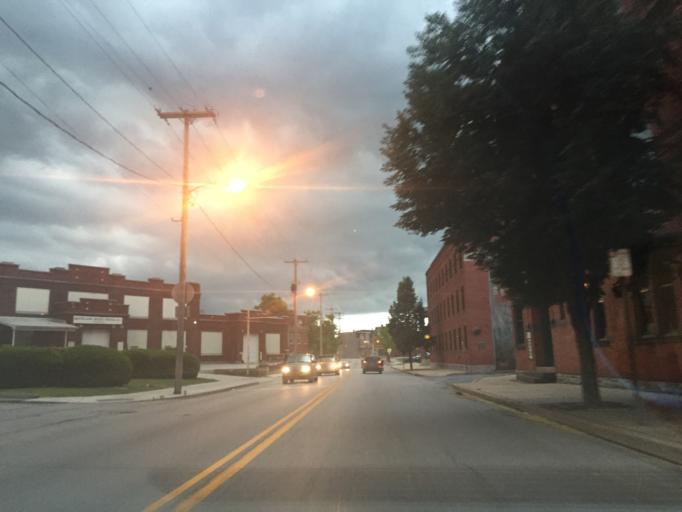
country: US
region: Pennsylvania
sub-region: York County
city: York
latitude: 39.9619
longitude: -76.7399
